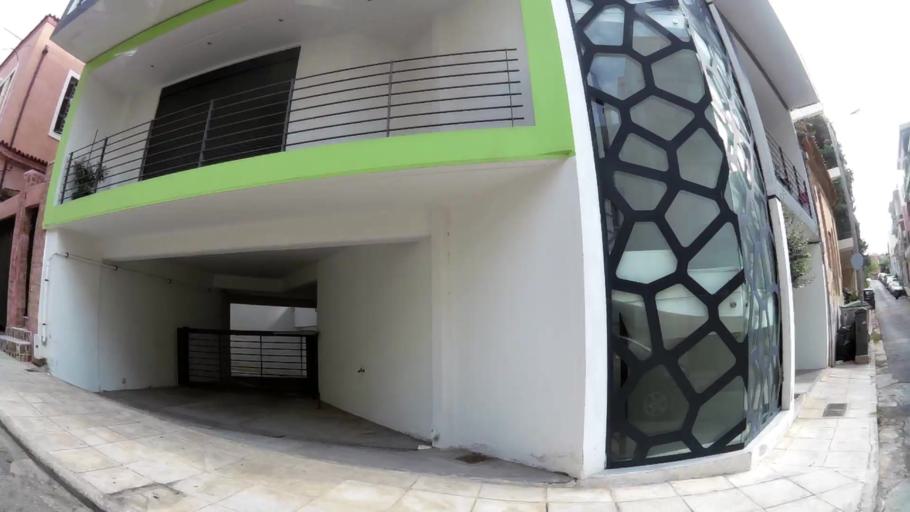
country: GR
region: Attica
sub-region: Nomarchia Athinas
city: Athens
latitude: 37.9657
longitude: 23.7154
